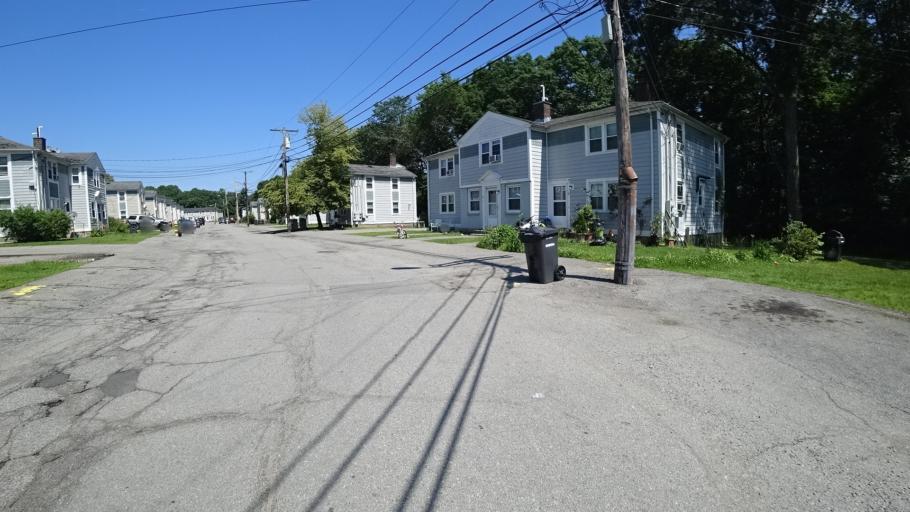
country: US
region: Massachusetts
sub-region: Norfolk County
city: Dedham
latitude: 42.2451
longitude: -71.1475
